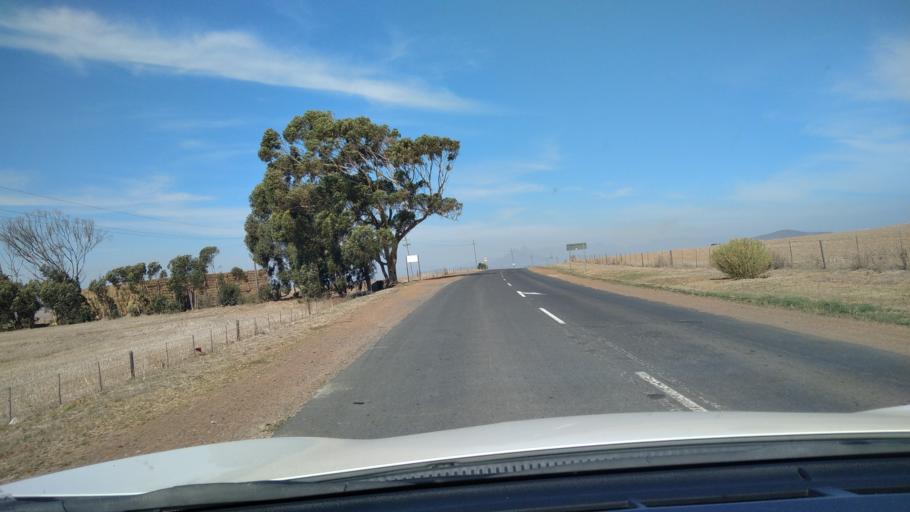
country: ZA
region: Western Cape
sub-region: City of Cape Town
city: Atlantis
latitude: -33.6691
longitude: 18.5843
